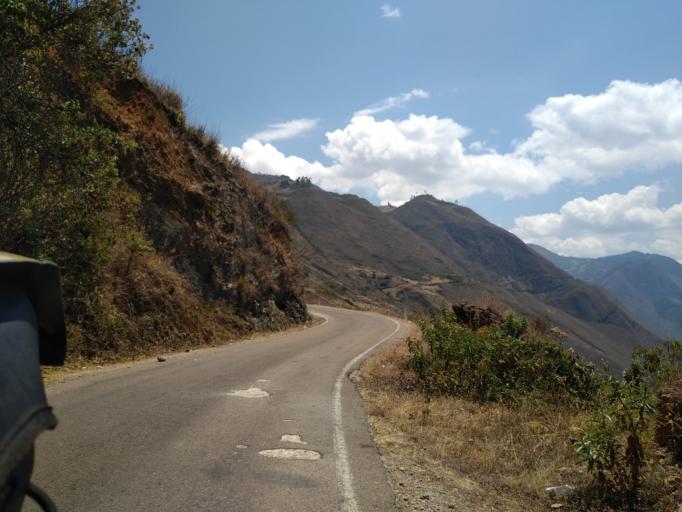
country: PE
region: Cajamarca
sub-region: Provincia de Celendin
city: Celendin
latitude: -6.8874
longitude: -78.0988
